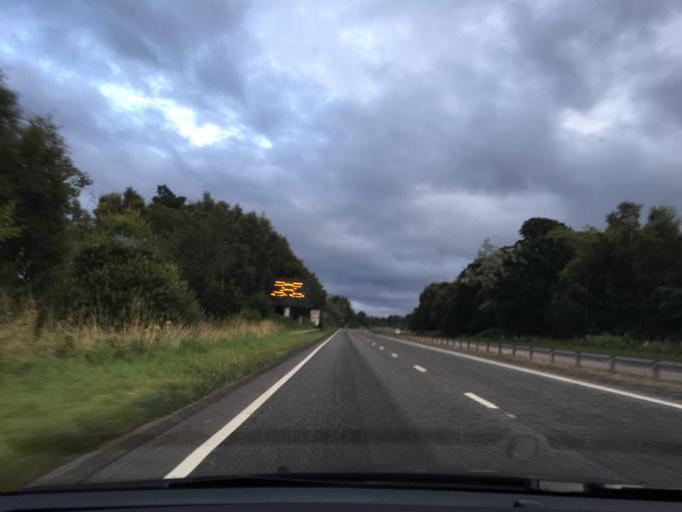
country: GB
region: Scotland
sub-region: Highland
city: Inverness
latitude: 57.4652
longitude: -4.1742
